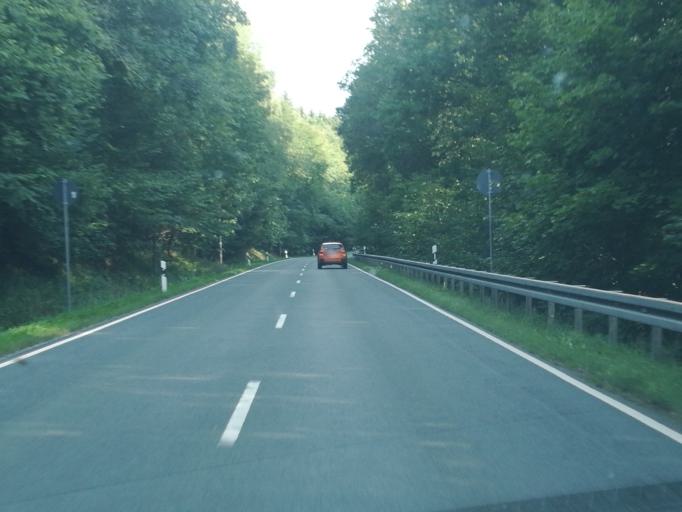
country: DE
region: Saxony
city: Adorf
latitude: 50.3337
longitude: 12.2521
